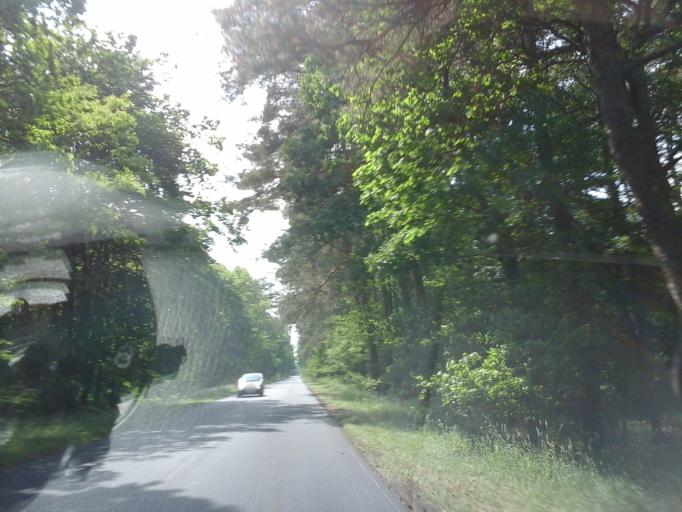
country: PL
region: West Pomeranian Voivodeship
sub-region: Powiat choszczenski
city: Drawno
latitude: 53.2058
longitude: 15.7127
